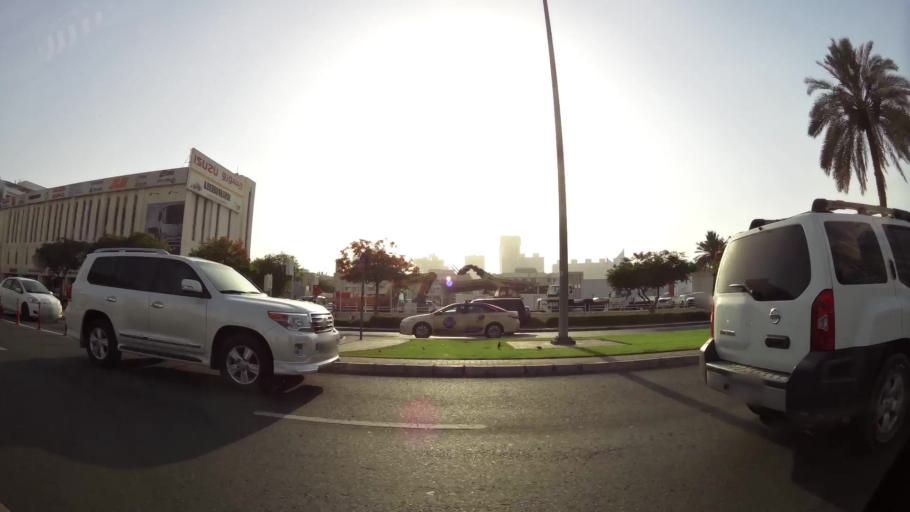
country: AE
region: Ash Shariqah
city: Sharjah
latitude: 25.2490
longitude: 55.3089
